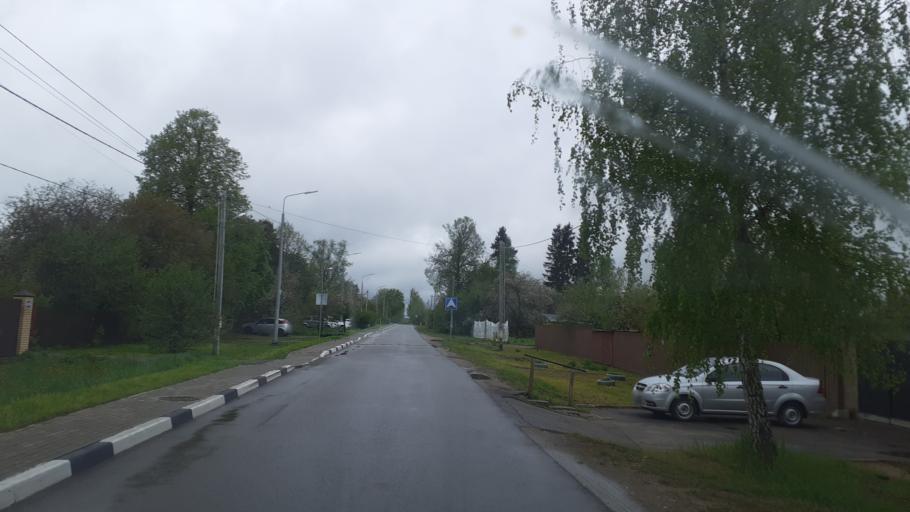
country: RU
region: Moskovskaya
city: Gorki Vtoryye
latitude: 55.7038
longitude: 37.2038
